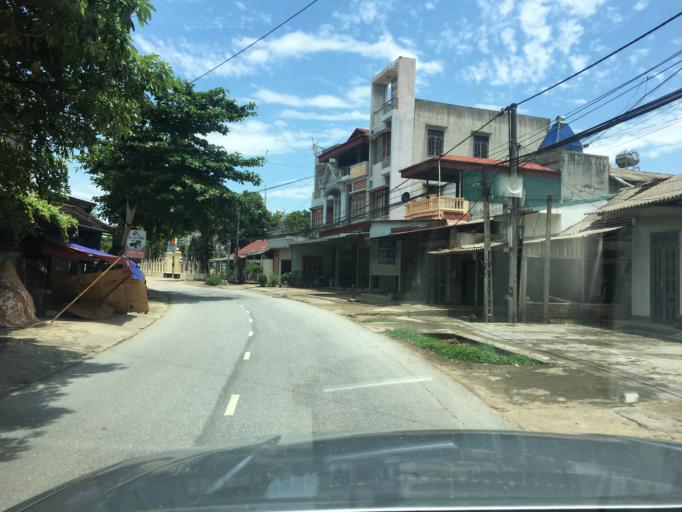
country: VN
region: Yen Bai
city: Son Thinh
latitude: 21.6402
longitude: 104.5011
